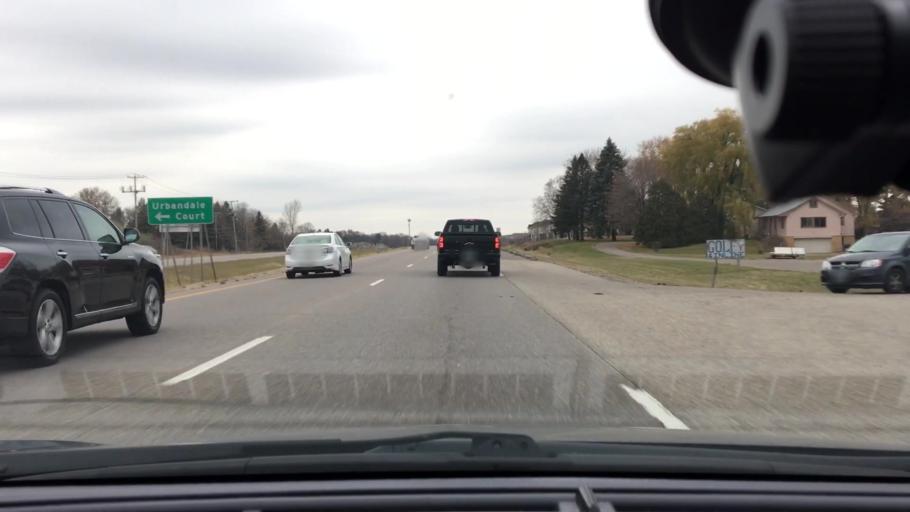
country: US
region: Minnesota
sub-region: Hennepin County
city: Plymouth
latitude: 45.0342
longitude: -93.5101
